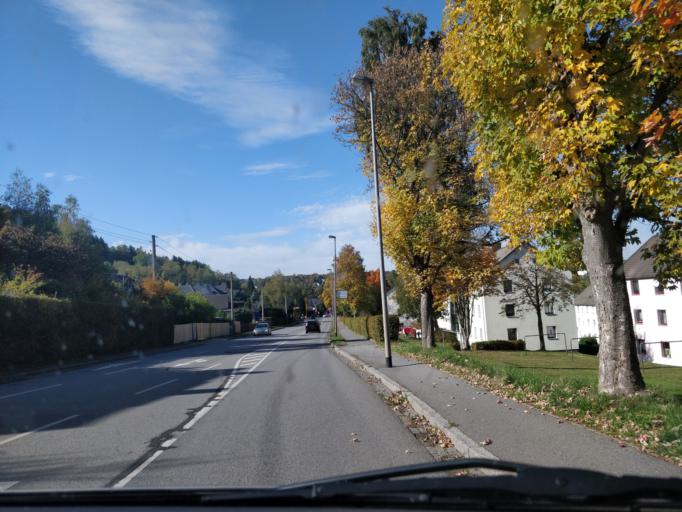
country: DE
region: Saxony
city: Schlema
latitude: 50.5969
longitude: 12.6630
